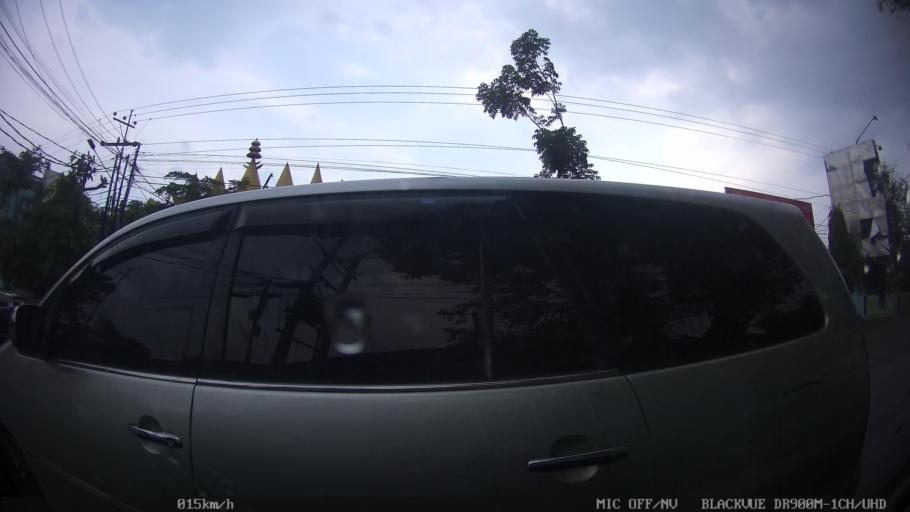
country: ID
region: Lampung
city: Bandarlampung
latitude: -5.4360
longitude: 105.2852
